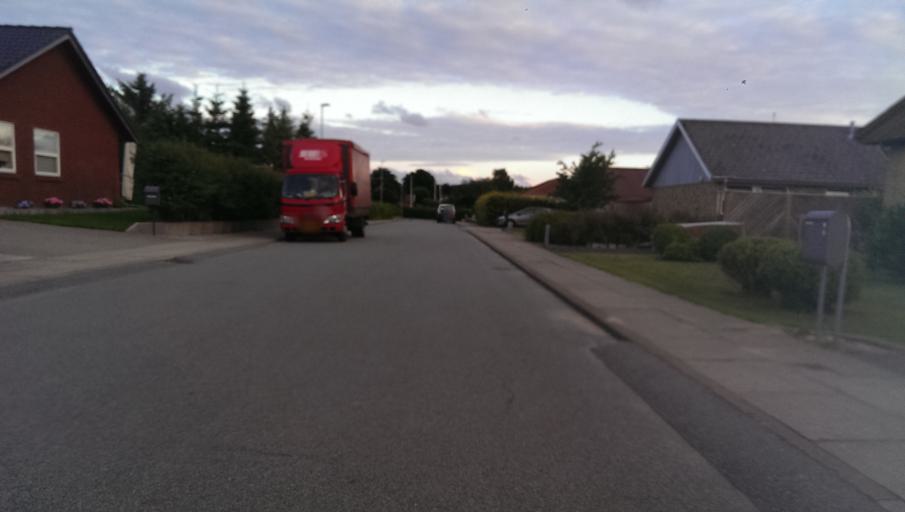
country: DK
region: South Denmark
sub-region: Esbjerg Kommune
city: Tjaereborg
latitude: 55.4706
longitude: 8.5723
